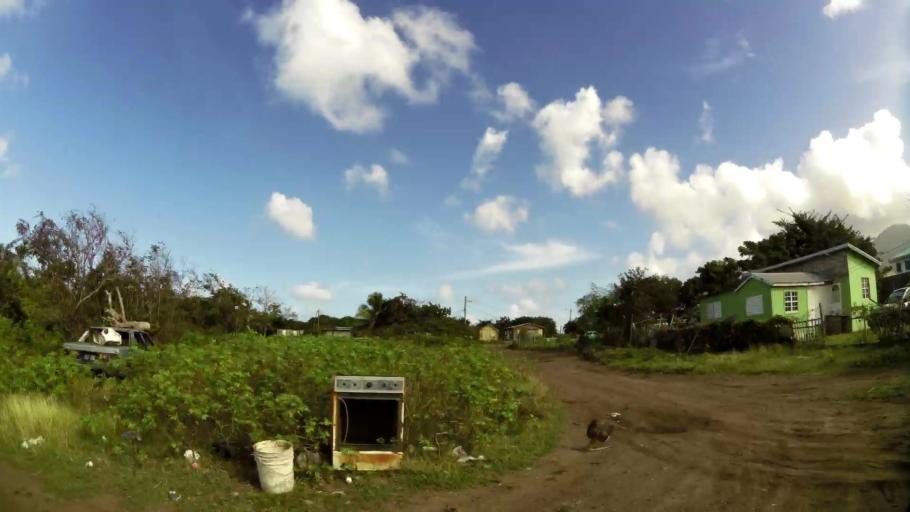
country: KN
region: Saint Paul Charlestown
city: Charlestown
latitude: 17.1294
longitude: -62.6284
